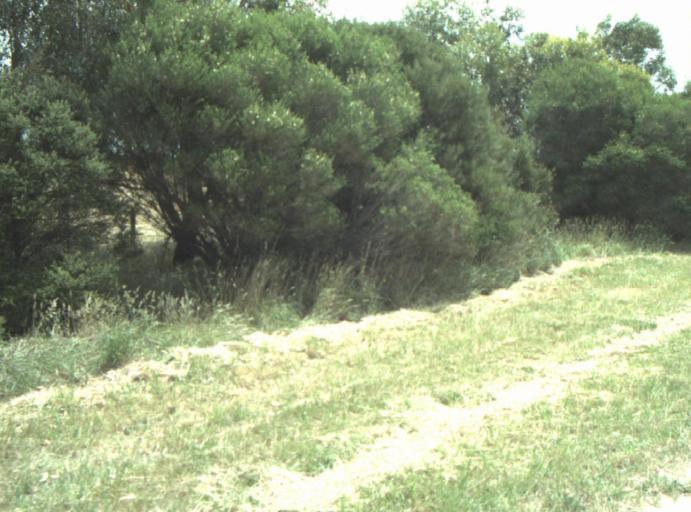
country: AU
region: Victoria
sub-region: Greater Geelong
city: Wandana Heights
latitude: -38.2380
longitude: 144.2971
